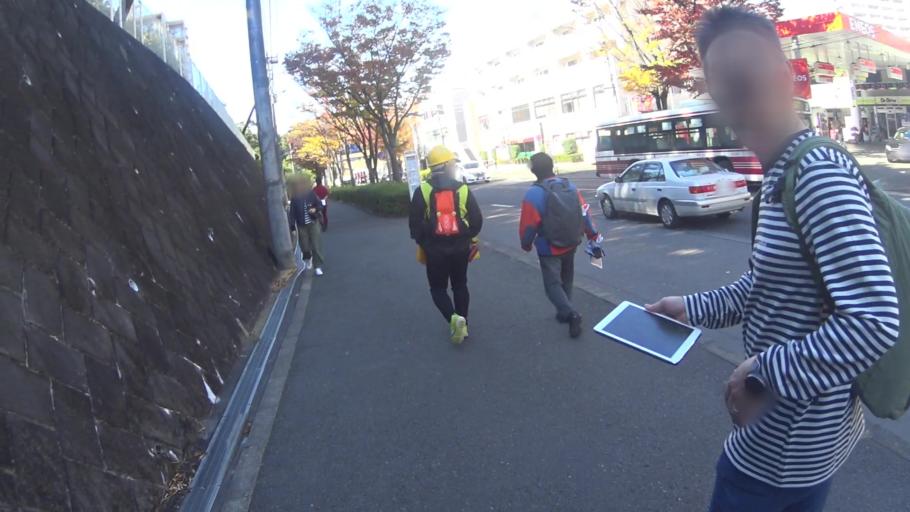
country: JP
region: Tokyo
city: Chofugaoka
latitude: 35.6045
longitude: 139.5008
